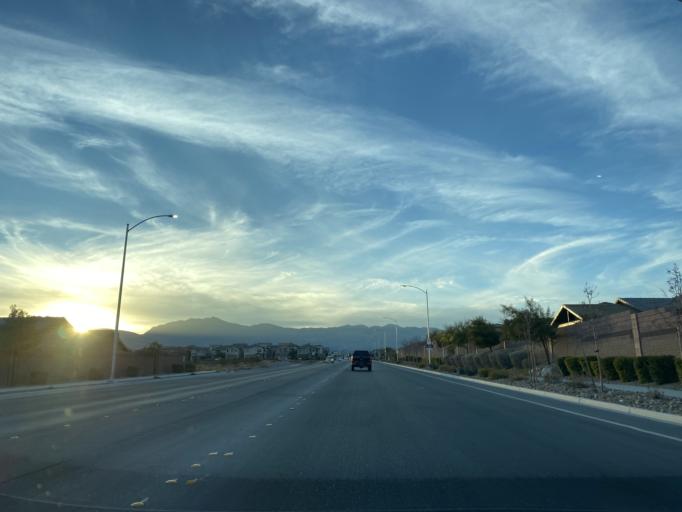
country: US
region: Nevada
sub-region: Clark County
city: Summerlin South
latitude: 36.2847
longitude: -115.3075
